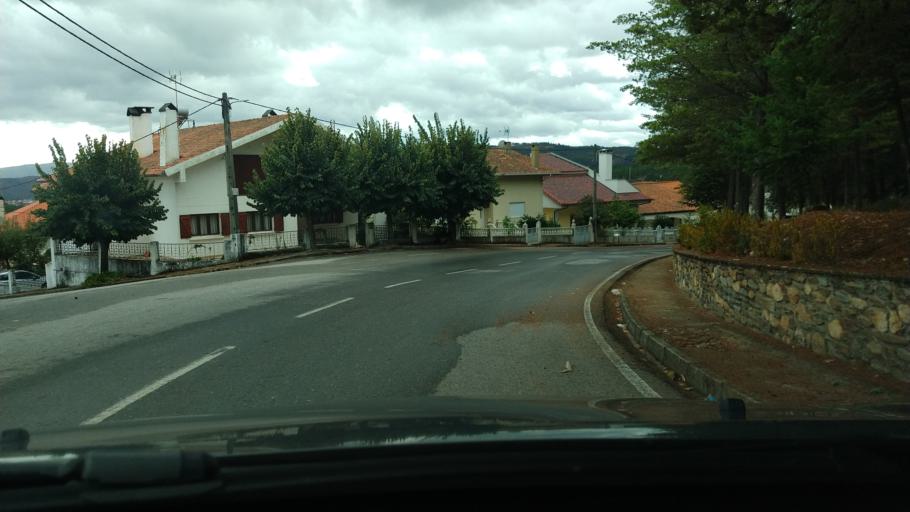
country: PT
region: Castelo Branco
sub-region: Covilha
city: Covilha
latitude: 40.2276
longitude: -7.6475
